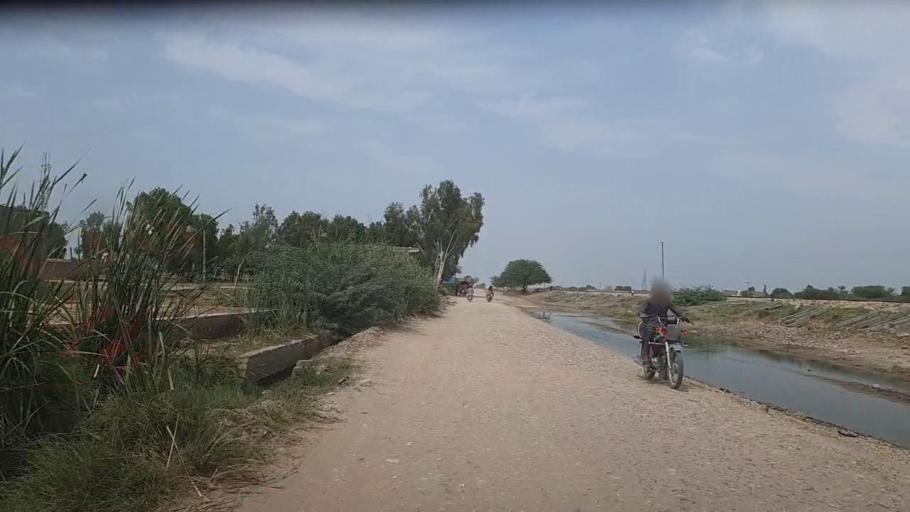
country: PK
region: Sindh
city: Bhiria
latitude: 26.8981
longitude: 68.2875
